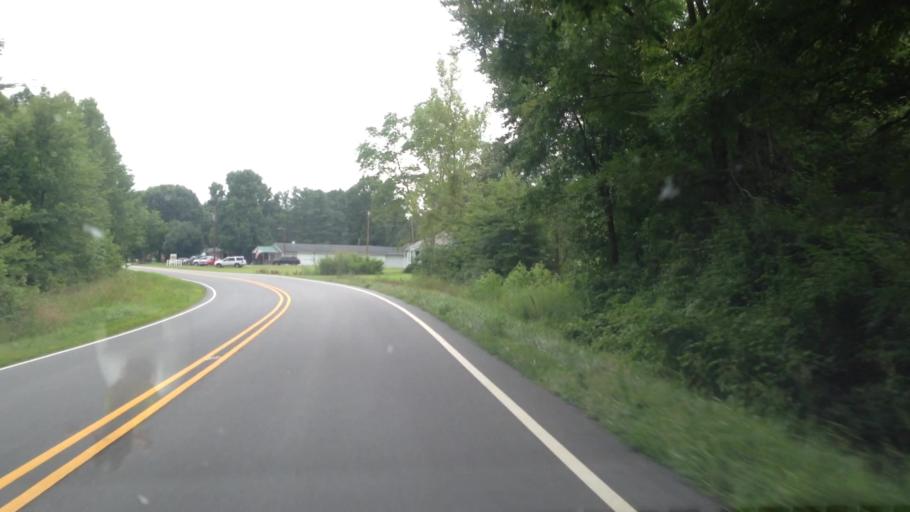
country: US
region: North Carolina
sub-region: Rockingham County
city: Mayodan
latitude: 36.4125
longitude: -80.0087
